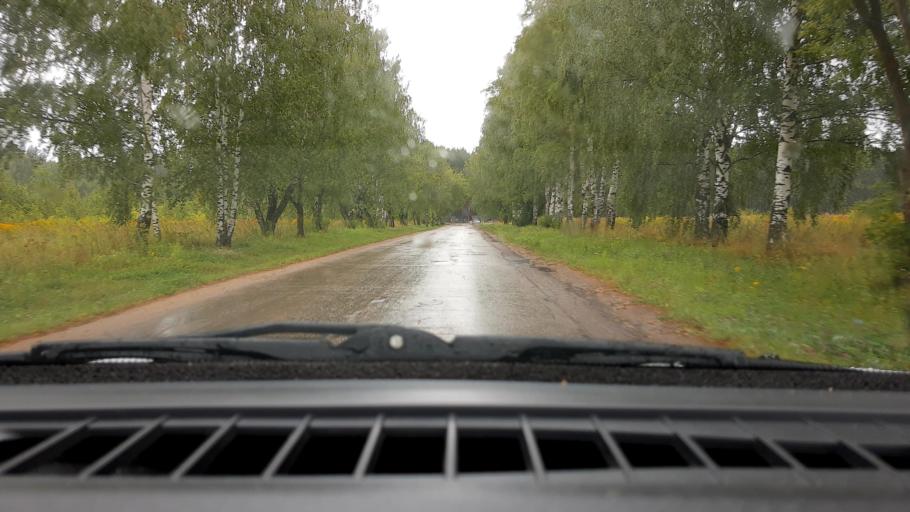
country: RU
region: Nizjnij Novgorod
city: Babino
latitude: 56.1414
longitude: 43.6515
